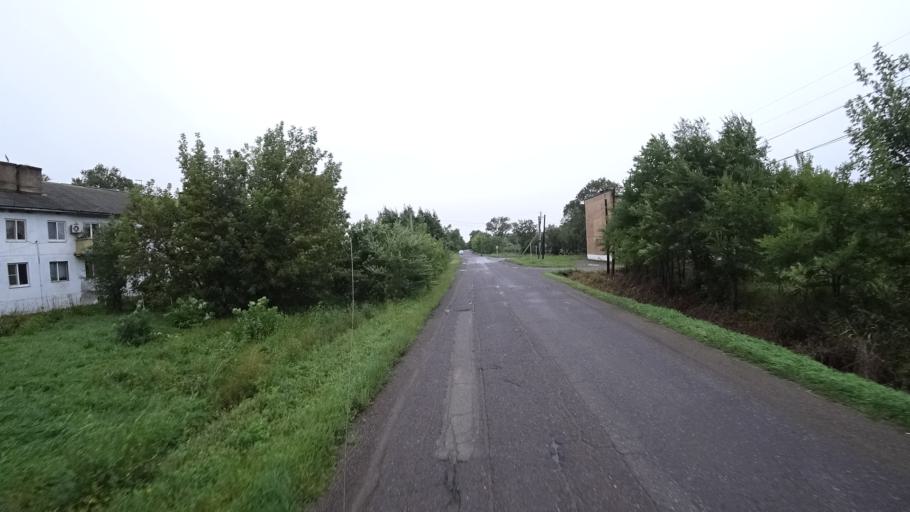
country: RU
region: Primorskiy
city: Chernigovka
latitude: 44.3395
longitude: 132.5729
